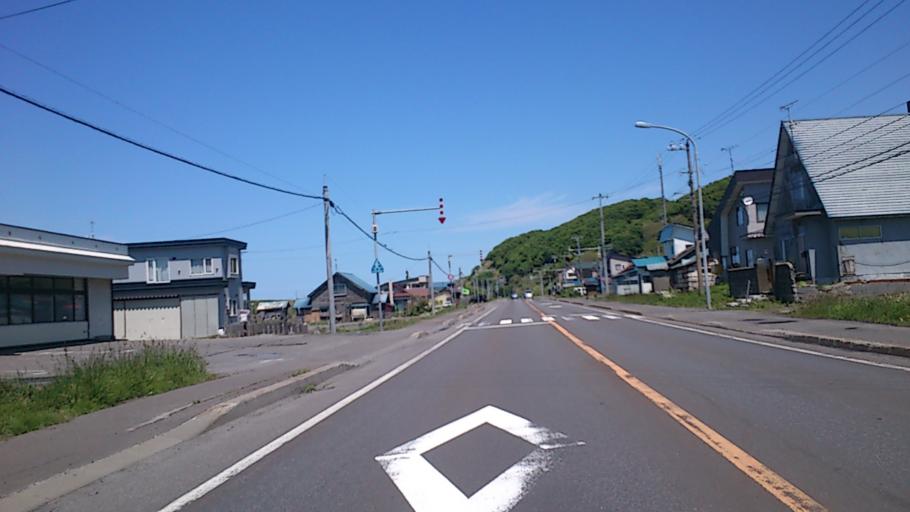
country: JP
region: Hokkaido
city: Rumoi
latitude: 43.9669
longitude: 141.6464
